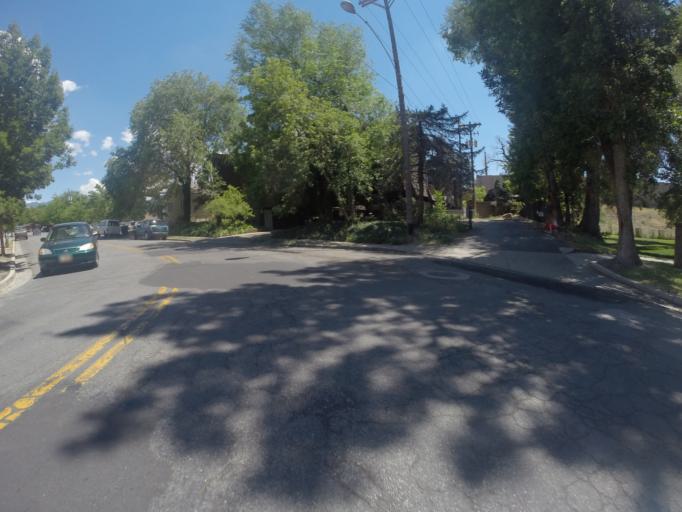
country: US
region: Utah
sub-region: Salt Lake County
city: Willard
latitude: 40.7207
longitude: -111.8596
